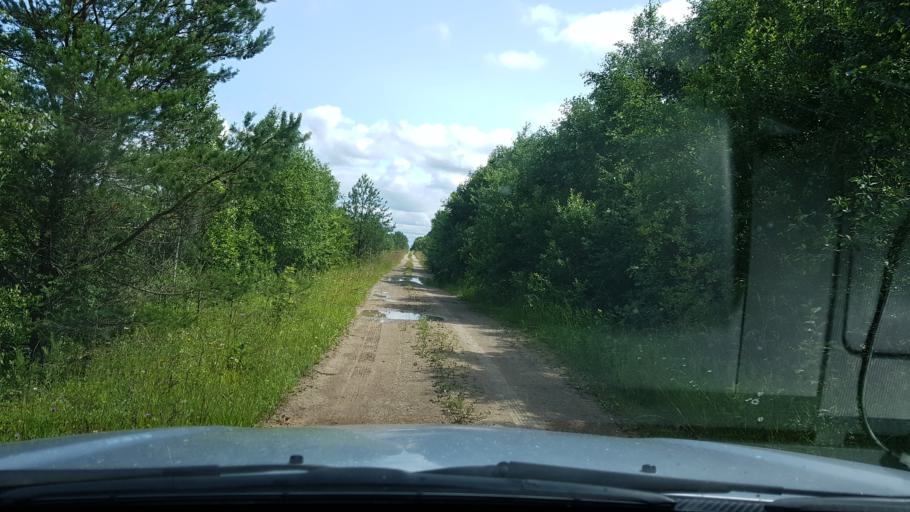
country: EE
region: Ida-Virumaa
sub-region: Sillamaee linn
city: Sillamae
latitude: 59.3628
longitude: 27.7905
